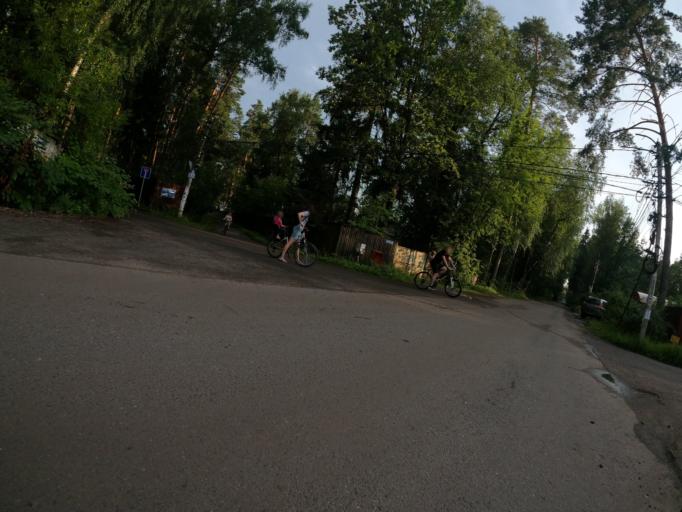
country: RU
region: Moskovskaya
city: Il'inskiy
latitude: 55.6392
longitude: 38.1120
